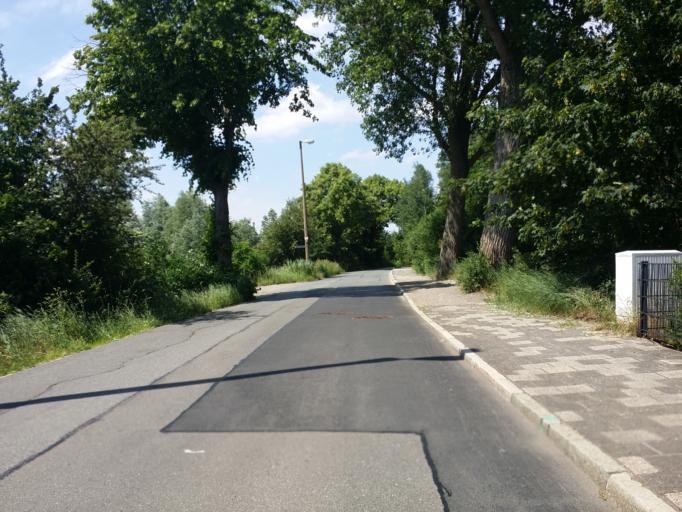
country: DE
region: Lower Saxony
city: Ritterhude
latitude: 53.1126
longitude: 8.7064
